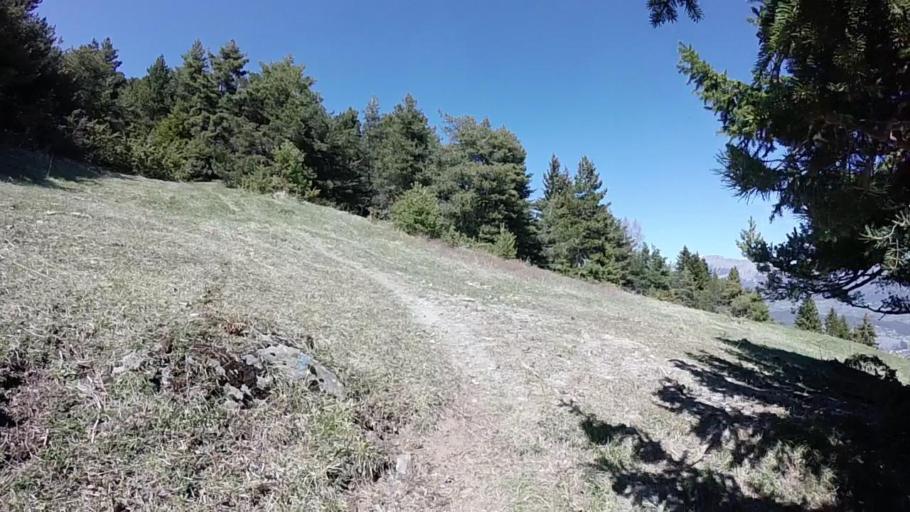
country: FR
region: Provence-Alpes-Cote d'Azur
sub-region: Departement des Alpes-de-Haute-Provence
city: Seyne-les-Alpes
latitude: 44.3319
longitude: 6.3029
